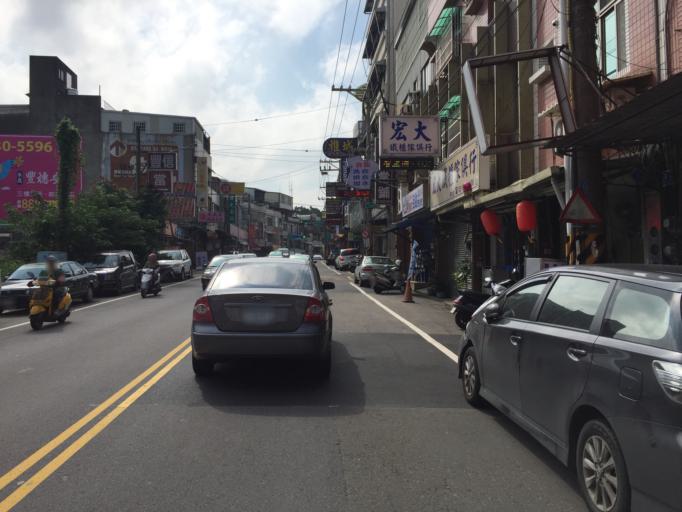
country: TW
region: Taiwan
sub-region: Hsinchu
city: Hsinchu
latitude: 24.7878
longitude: 120.9672
